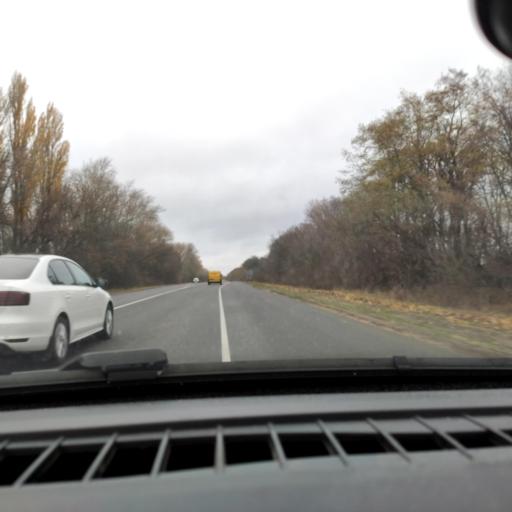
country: RU
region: Voronezj
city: Kolodeznyy
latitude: 51.2541
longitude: 39.0537
